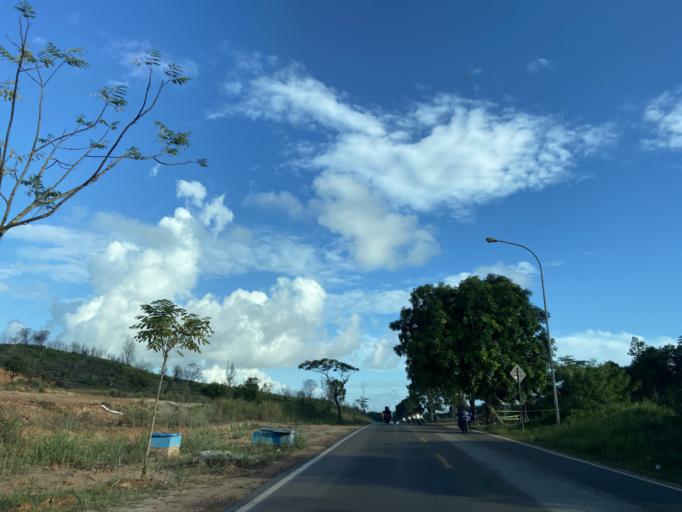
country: SG
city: Singapore
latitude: 1.0190
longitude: 104.0148
